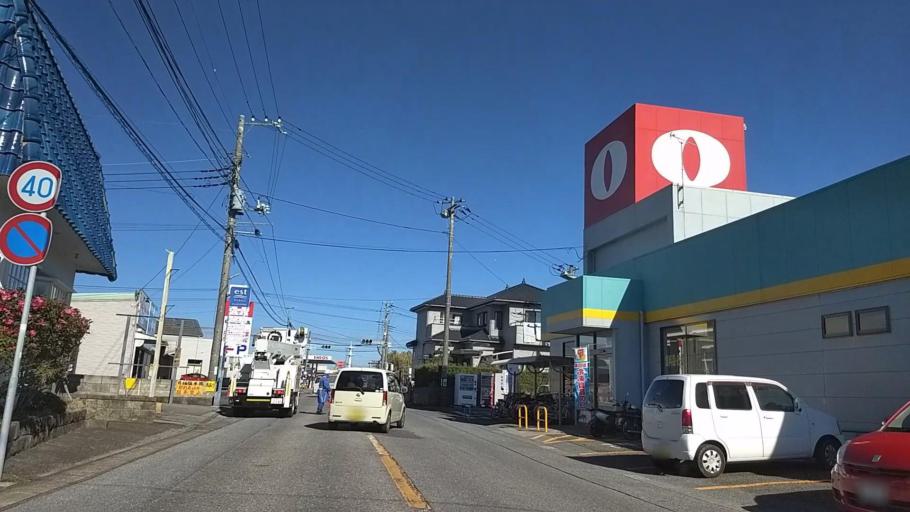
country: JP
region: Chiba
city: Tateyama
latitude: 34.9637
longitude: 139.9576
